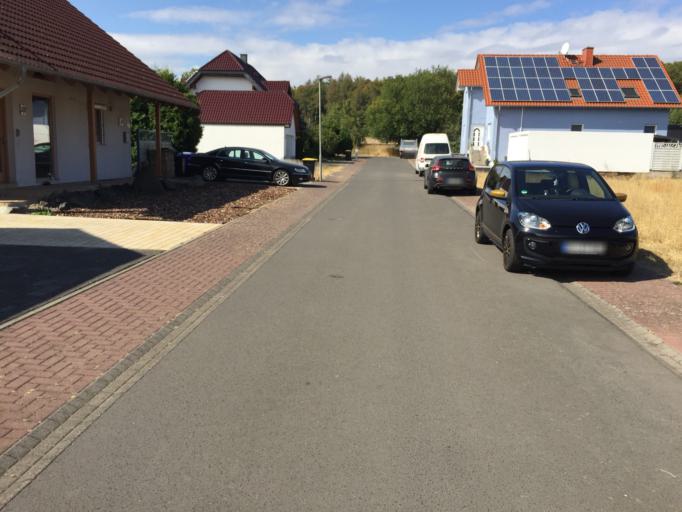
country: DE
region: Hesse
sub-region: Regierungsbezirk Giessen
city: Hungen
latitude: 50.4630
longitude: 8.8966
